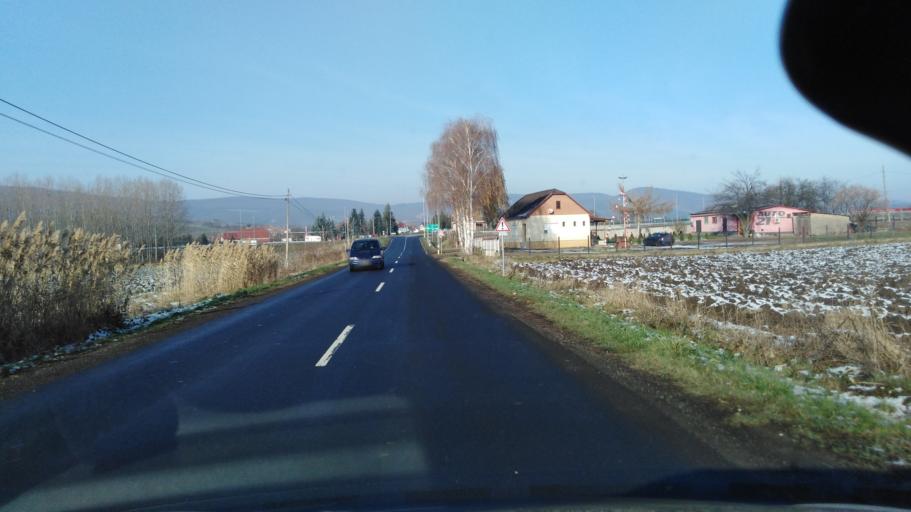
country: HU
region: Nograd
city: Paszto
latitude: 47.9429
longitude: 19.7038
